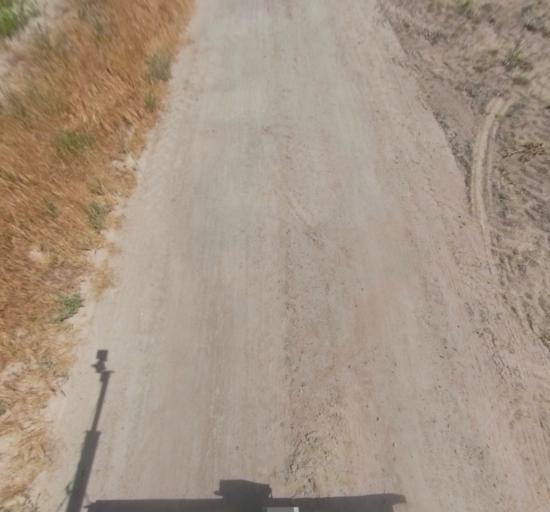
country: US
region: California
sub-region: Madera County
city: Parkwood
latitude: 36.8542
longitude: -120.2010
